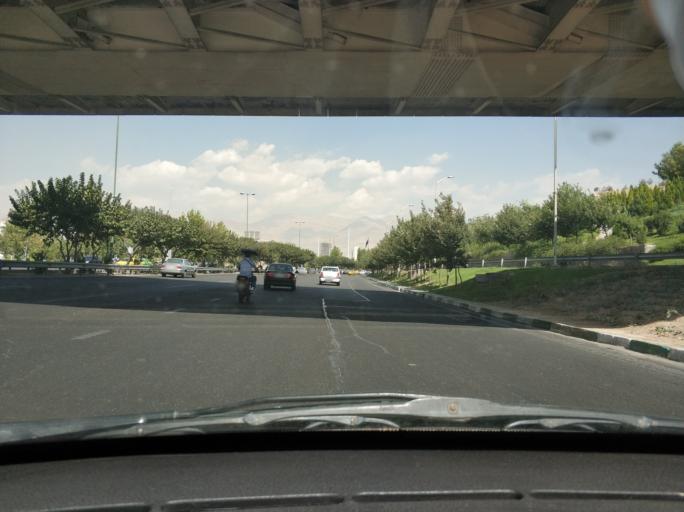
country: IR
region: Tehran
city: Tehran
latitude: 35.7439
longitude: 51.3698
